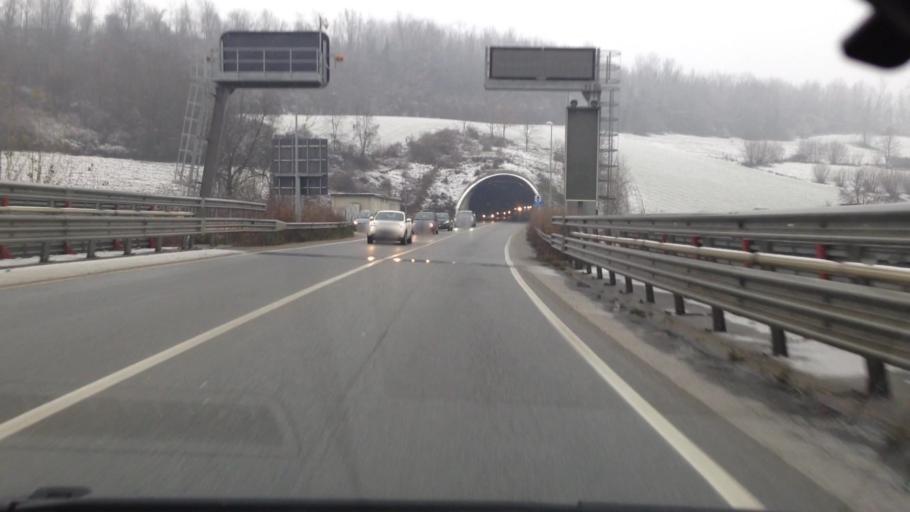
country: IT
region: Piedmont
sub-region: Provincia di Asti
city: Isola d'Asti
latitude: 44.8425
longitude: 8.1924
